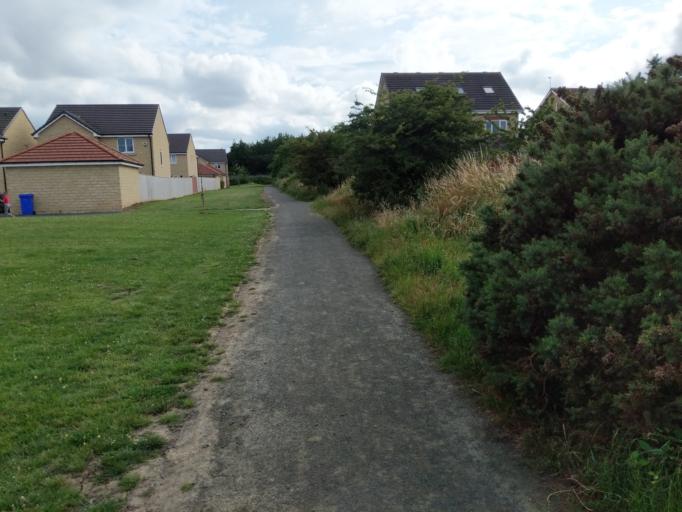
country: GB
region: England
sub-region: Northumberland
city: Blyth
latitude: 55.1210
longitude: -1.5485
